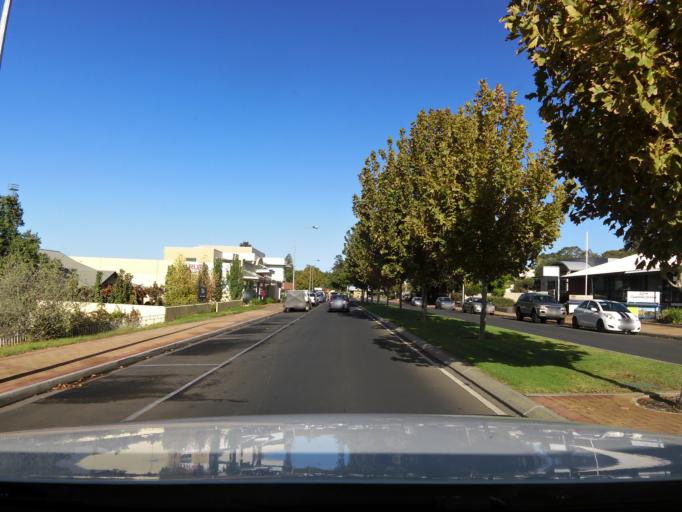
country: AU
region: South Australia
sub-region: Berri and Barmera
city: Berri
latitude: -34.2841
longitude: 140.6037
